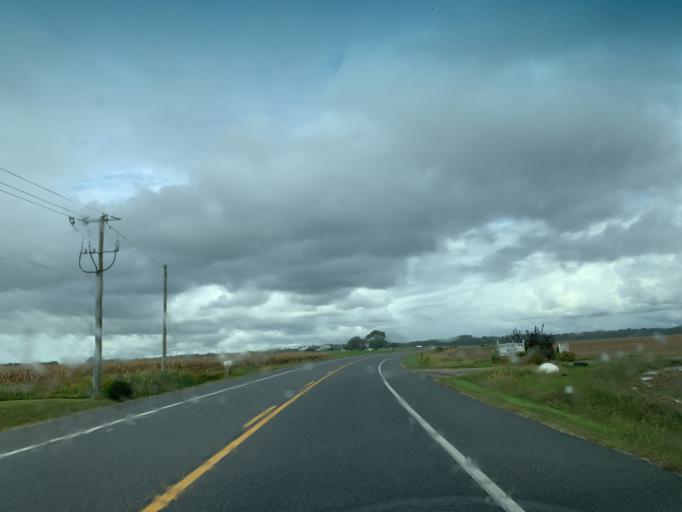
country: US
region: Maryland
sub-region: Caroline County
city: Ridgely
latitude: 38.9957
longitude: -75.8763
